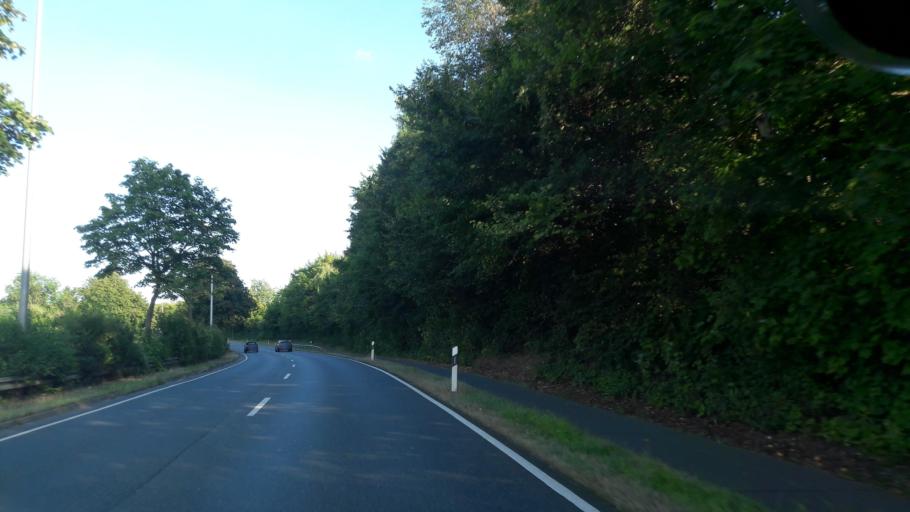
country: DE
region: Lower Saxony
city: Giesen
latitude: 52.1577
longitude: 9.9078
